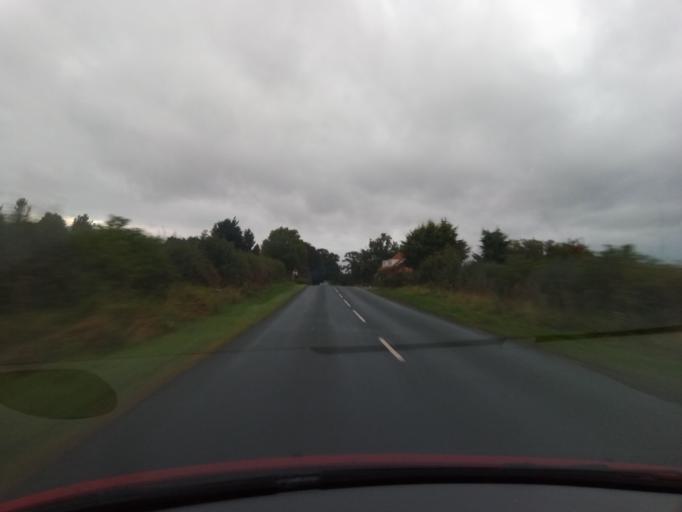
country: GB
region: England
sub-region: Darlington
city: High Coniscliffe
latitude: 54.5139
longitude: -1.6715
